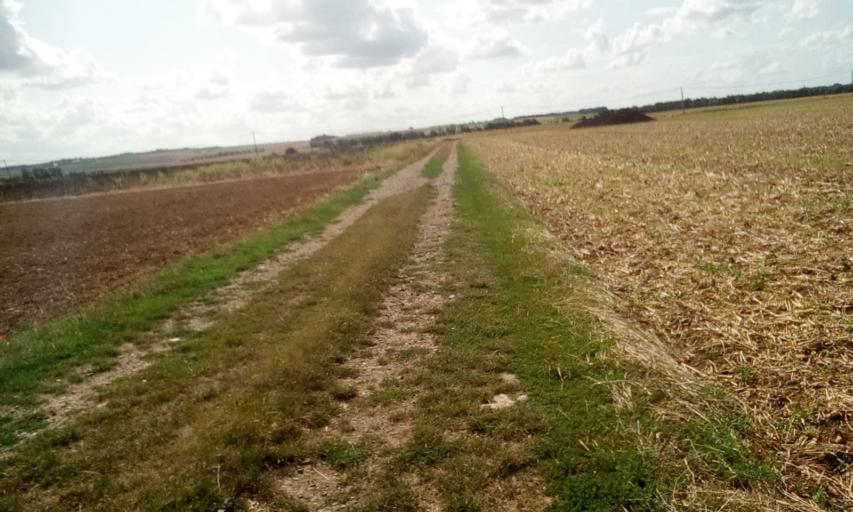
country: FR
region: Lower Normandy
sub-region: Departement du Calvados
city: Saint-Sylvain
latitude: 49.0726
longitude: -0.2186
